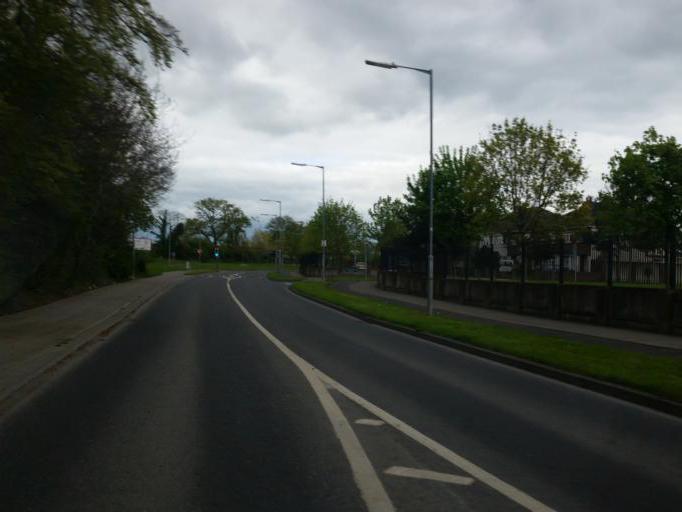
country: IE
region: Leinster
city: Hartstown
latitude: 53.3927
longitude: -6.4316
